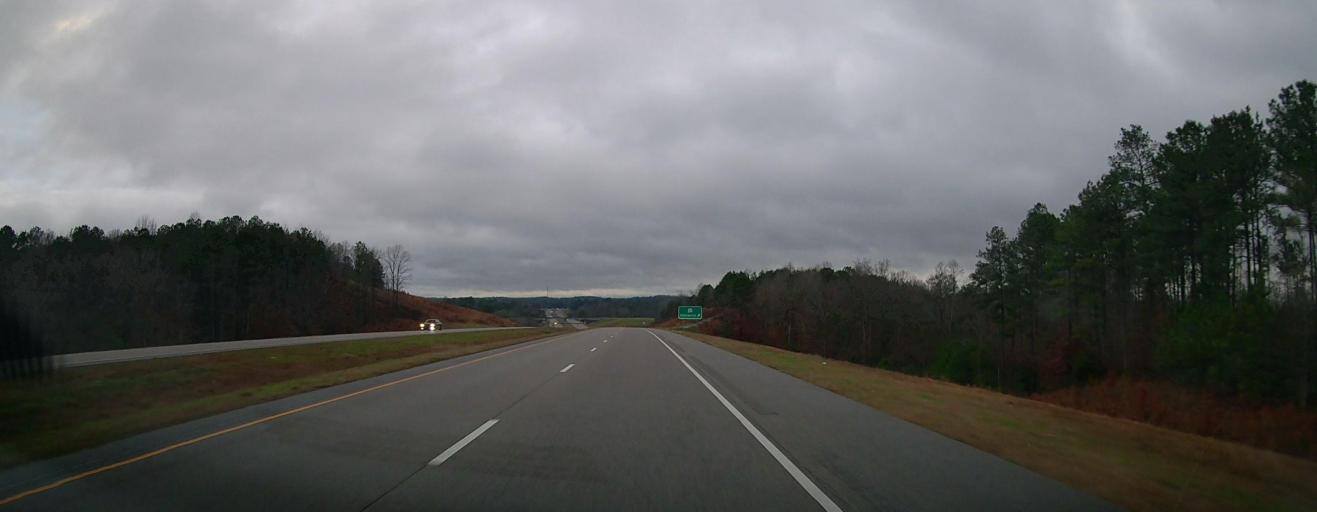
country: US
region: Alabama
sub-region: Bibb County
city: Centreville
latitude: 32.9564
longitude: -87.1245
